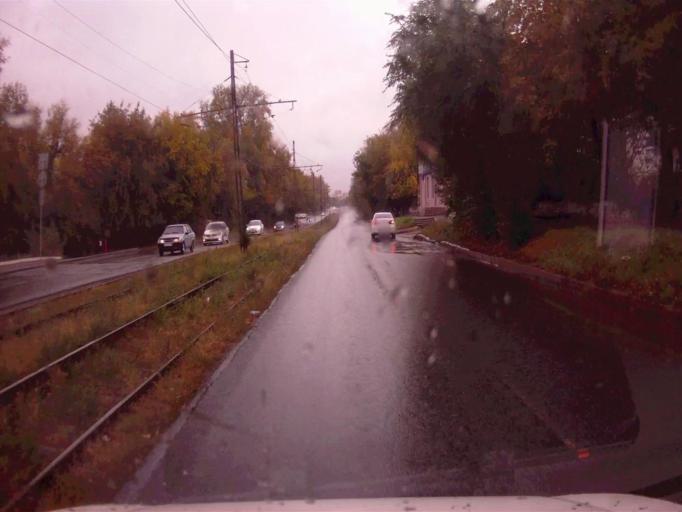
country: RU
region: Chelyabinsk
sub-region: Gorod Chelyabinsk
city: Chelyabinsk
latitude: 55.1782
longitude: 61.4148
